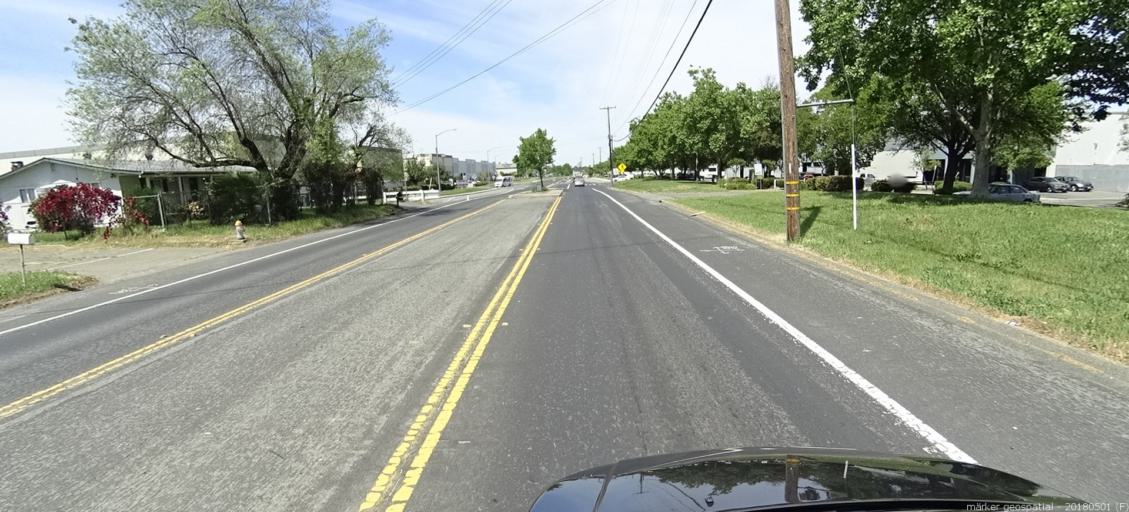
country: US
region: California
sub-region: Sacramento County
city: Rio Linda
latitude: 38.6568
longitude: -121.4291
